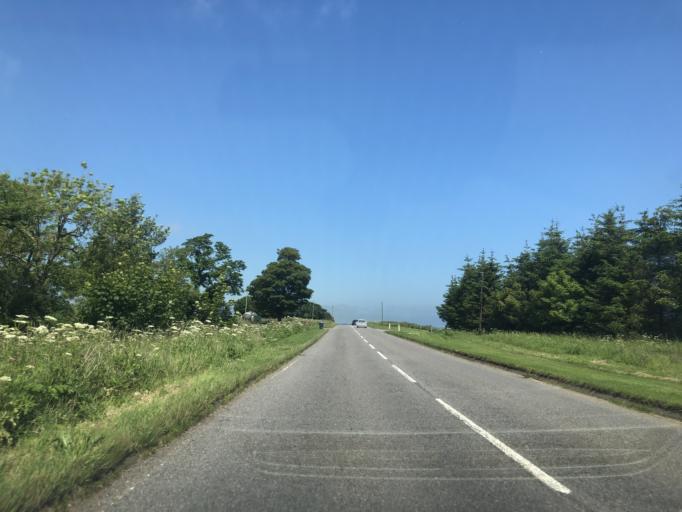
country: GB
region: Scotland
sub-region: Aberdeenshire
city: Stonehaven
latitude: 56.9338
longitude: -2.2079
